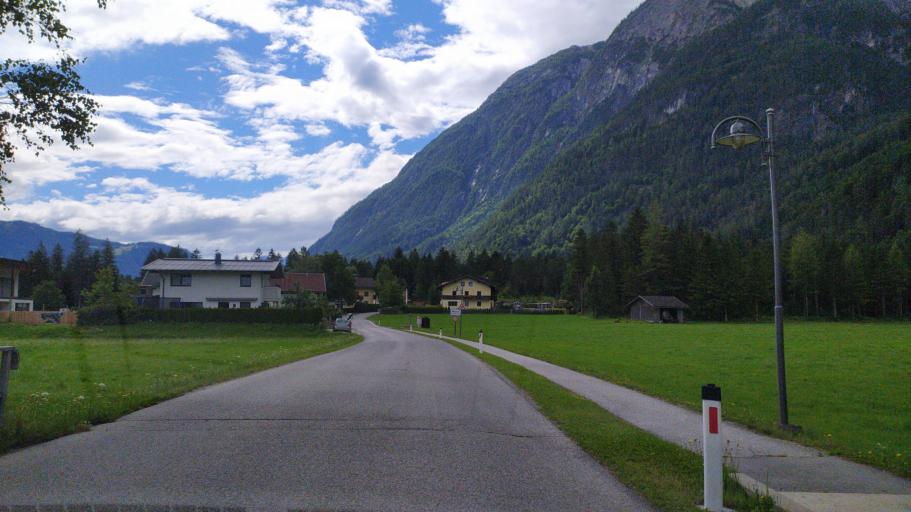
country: AT
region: Tyrol
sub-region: Politischer Bezirk Lienz
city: Lavant
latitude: 46.7920
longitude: 12.8584
